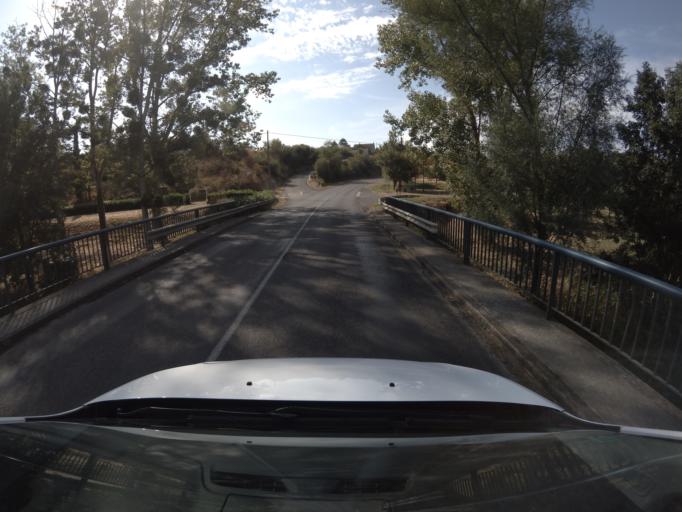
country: FR
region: Poitou-Charentes
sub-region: Departement des Deux-Sevres
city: Mauze-Thouarsais
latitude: 47.0032
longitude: -0.3377
